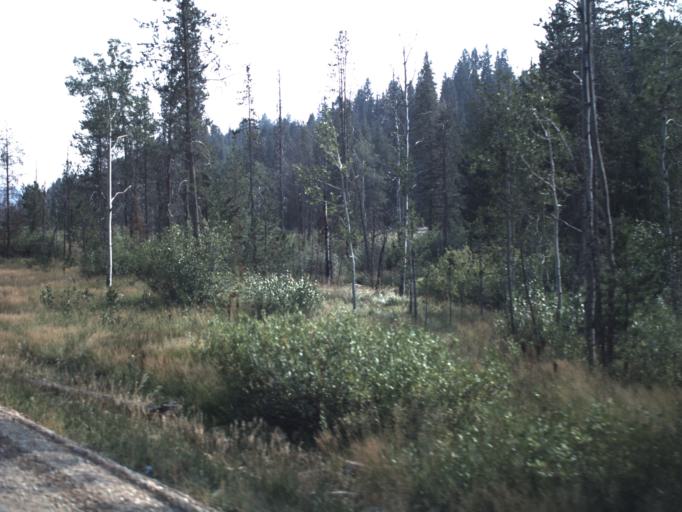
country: US
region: Utah
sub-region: Summit County
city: Francis
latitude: 40.6160
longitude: -111.1310
